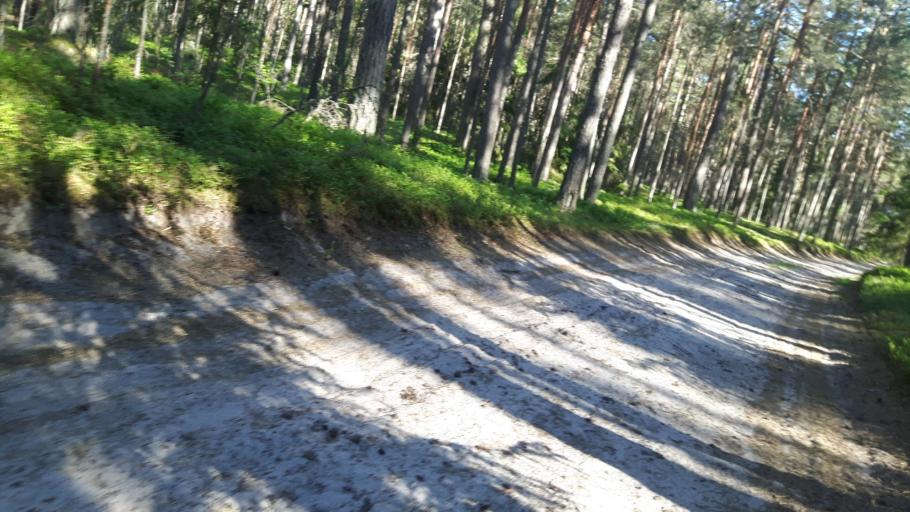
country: LV
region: Salacgrivas
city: Salacgriva
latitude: 57.7124
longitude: 24.3510
